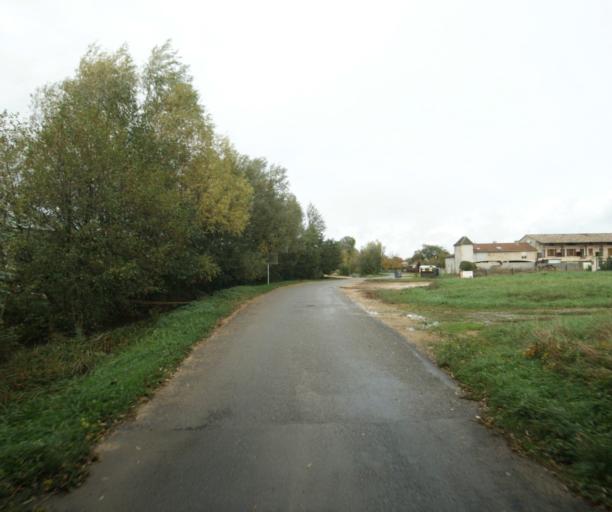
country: FR
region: Rhone-Alpes
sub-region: Departement de l'Ain
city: Pont-de-Vaux
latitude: 46.4741
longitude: 4.8969
